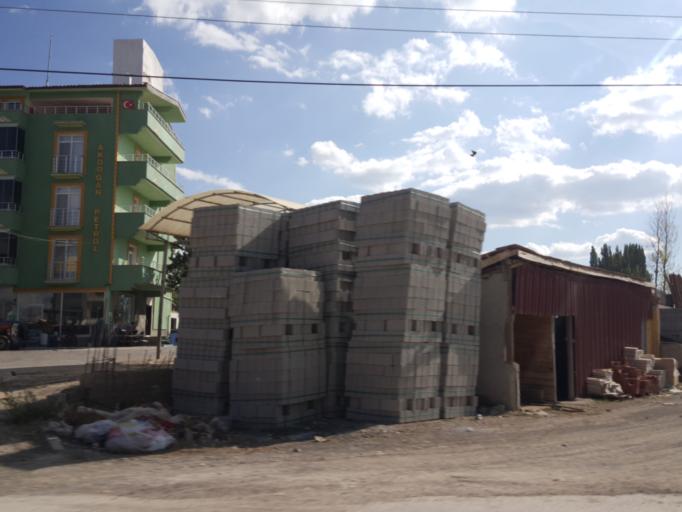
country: TR
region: Tokat
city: Sulusaray
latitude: 39.9958
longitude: 36.0911
